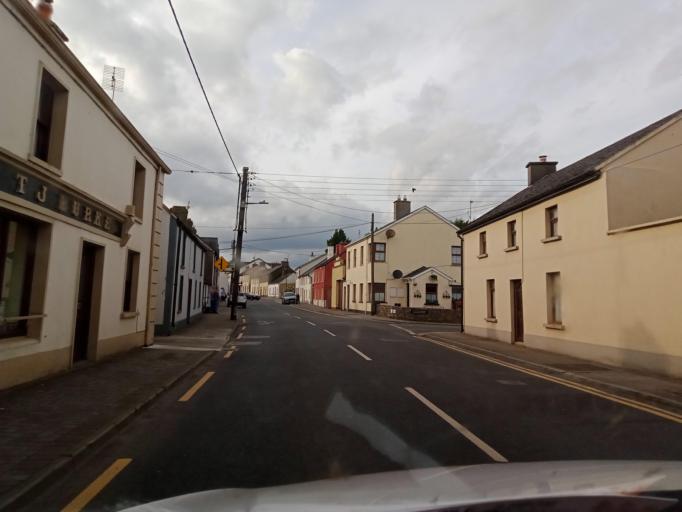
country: IE
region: Leinster
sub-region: Laois
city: Mountrath
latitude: 52.9995
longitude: -7.4716
